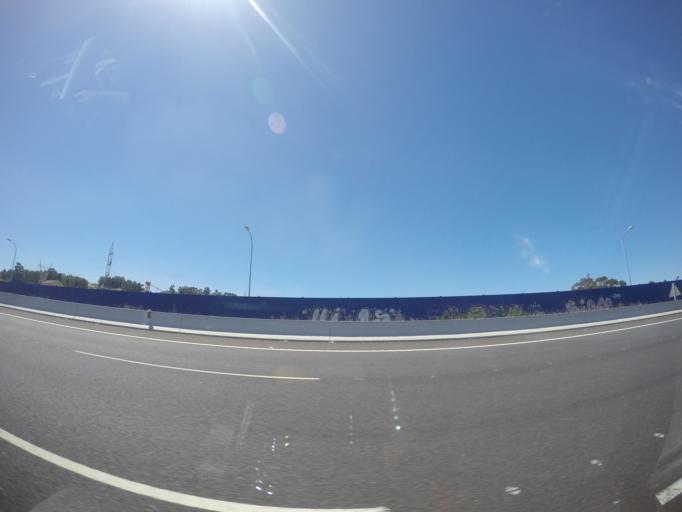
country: ES
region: Galicia
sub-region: Provincia da Coruna
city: A Coruna
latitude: 43.3395
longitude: -8.4231
